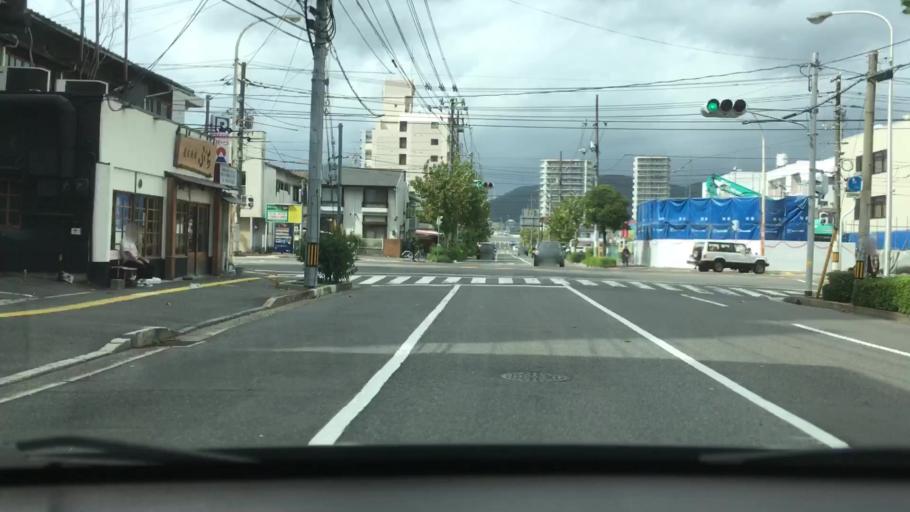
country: JP
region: Hiroshima
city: Hiroshima-shi
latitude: 34.3813
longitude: 132.4405
